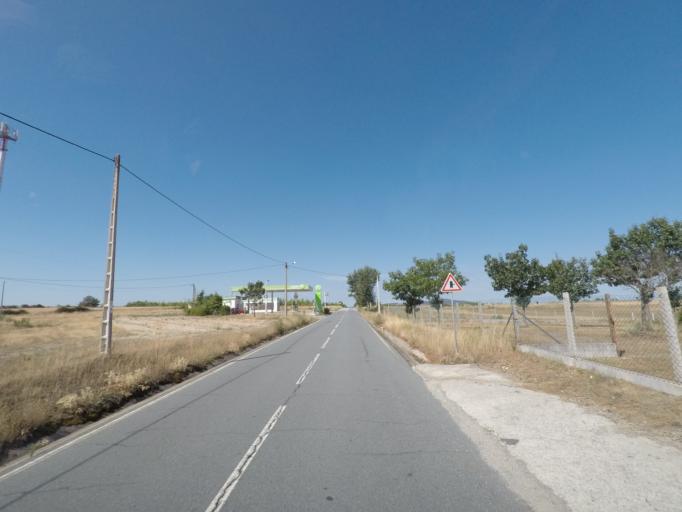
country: ES
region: Castille and Leon
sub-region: Provincia de Salamanca
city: Villarino de los Aires
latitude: 41.3664
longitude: -6.5023
